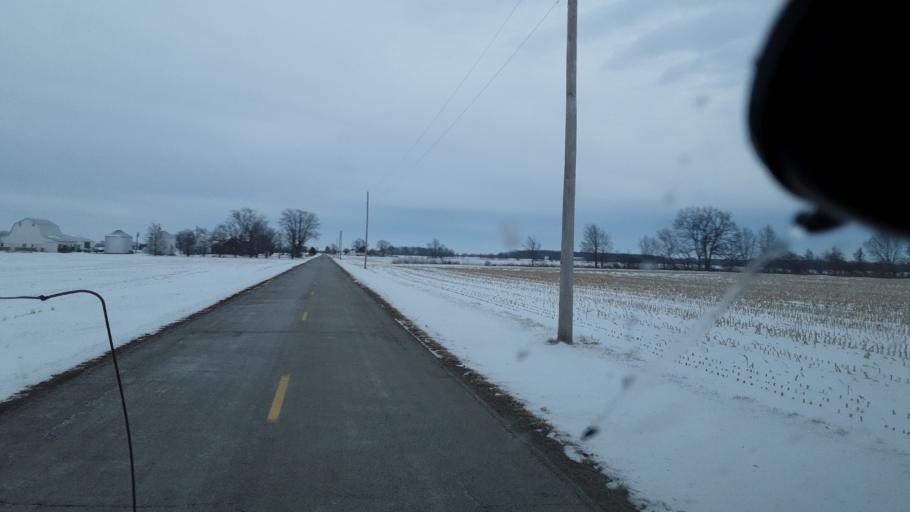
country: US
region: Ohio
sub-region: Madison County
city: Bethel
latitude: 39.7123
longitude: -83.3523
